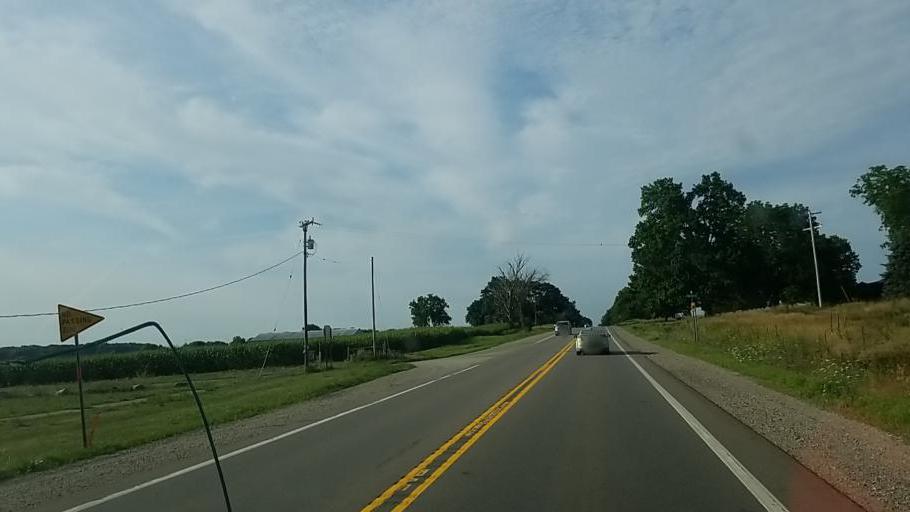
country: US
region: Michigan
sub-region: Ionia County
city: Ionia
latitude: 42.9115
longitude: -85.0749
